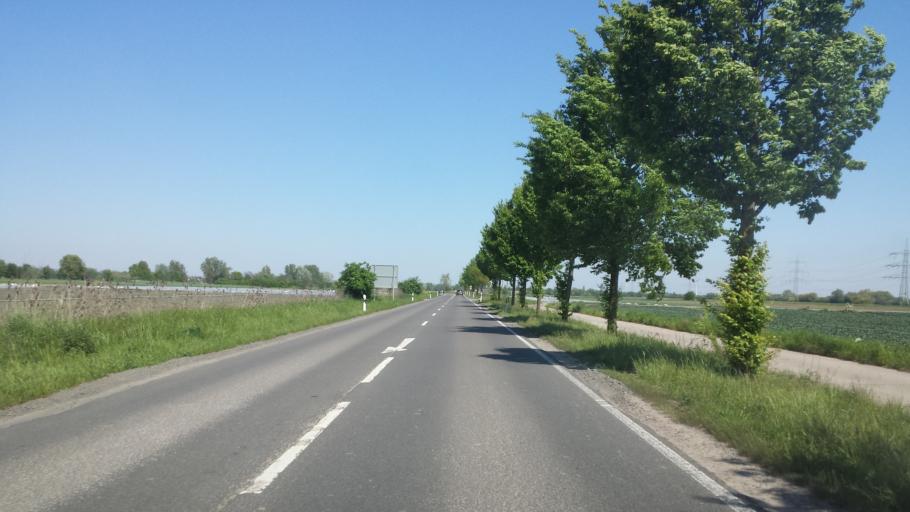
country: DE
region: Rheinland-Pfalz
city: Maxdorf
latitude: 49.4850
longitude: 8.3042
